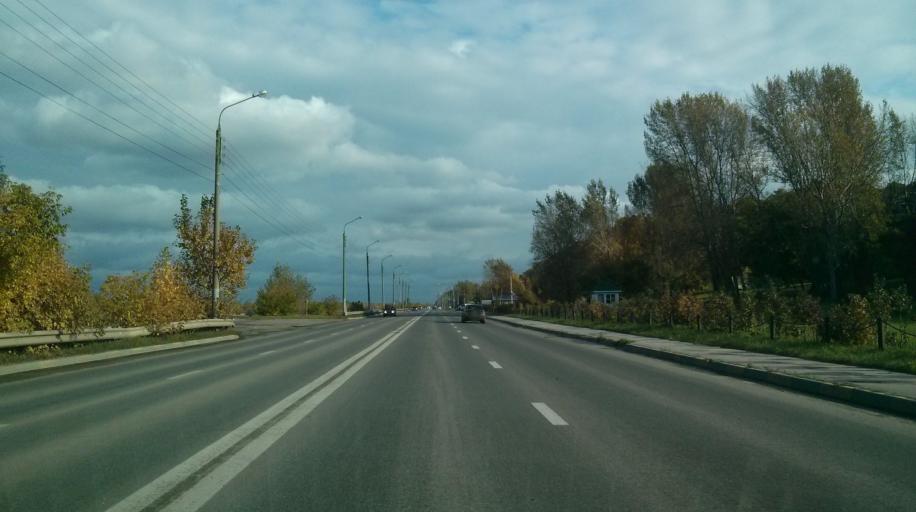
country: RU
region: Nizjnij Novgorod
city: Bor
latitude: 56.3247
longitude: 44.0518
